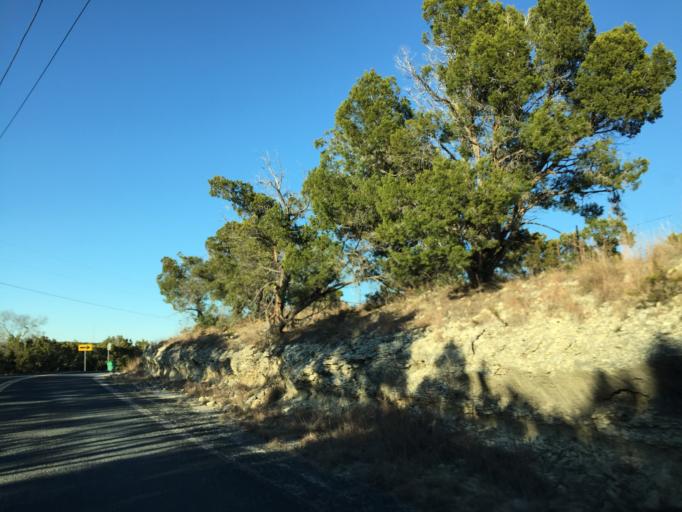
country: US
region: Texas
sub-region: Travis County
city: Lago Vista
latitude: 30.5214
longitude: -98.0893
